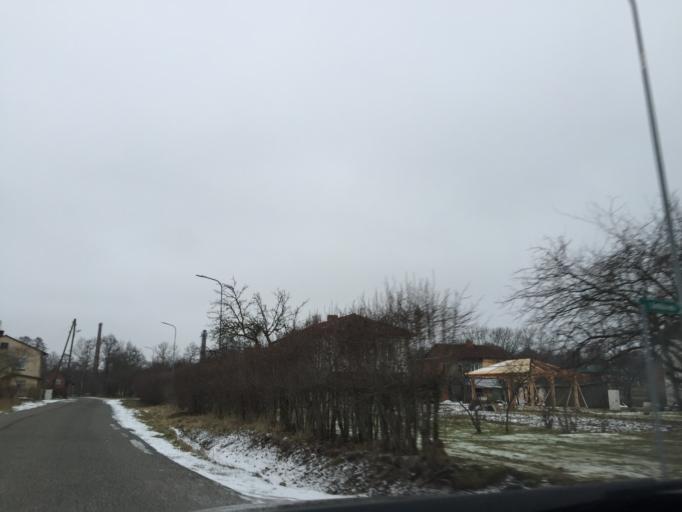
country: LV
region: Saulkrastu
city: Saulkrasti
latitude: 57.4920
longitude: 24.3886
